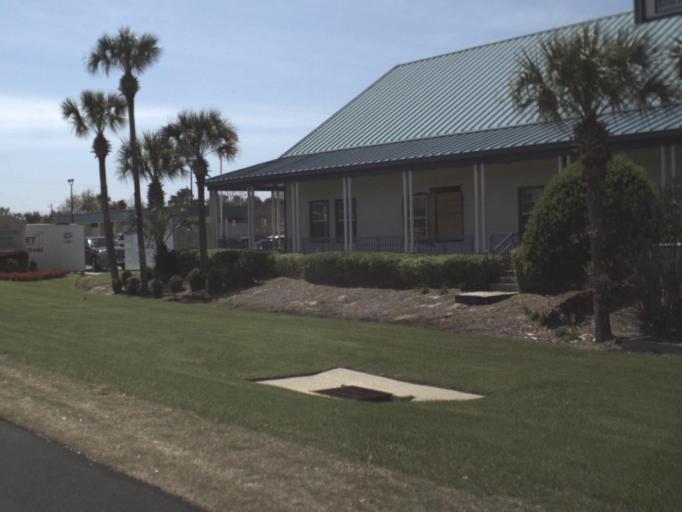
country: US
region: Florida
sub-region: Bay County
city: Laguna Beach
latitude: 30.2295
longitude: -85.8881
